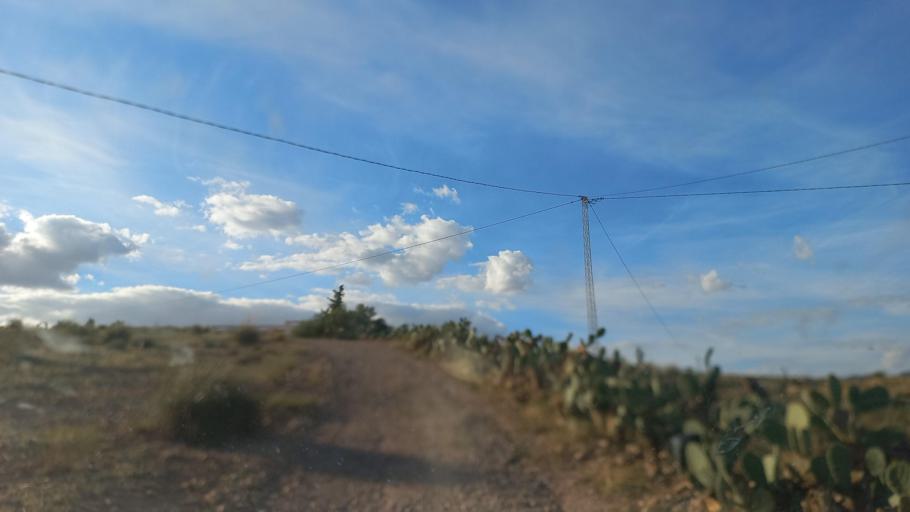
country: TN
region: Al Qasrayn
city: Sbiba
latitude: 35.3814
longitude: 9.0178
